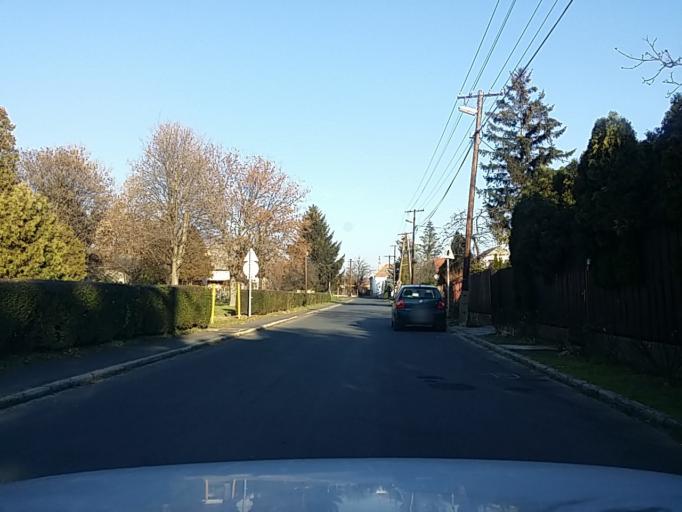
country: HU
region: Veszprem
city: Badacsonytomaj
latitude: 46.8075
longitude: 17.5149
